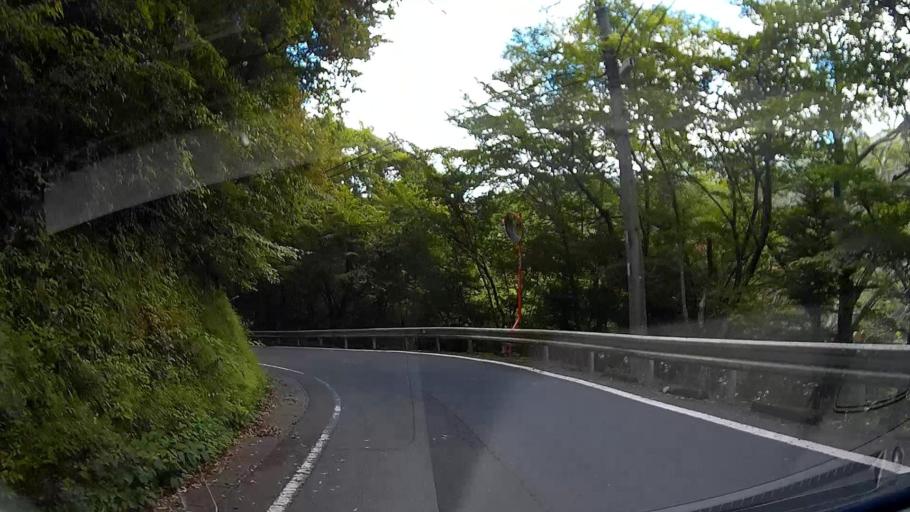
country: JP
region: Shizuoka
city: Shizuoka-shi
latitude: 35.2351
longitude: 138.2529
